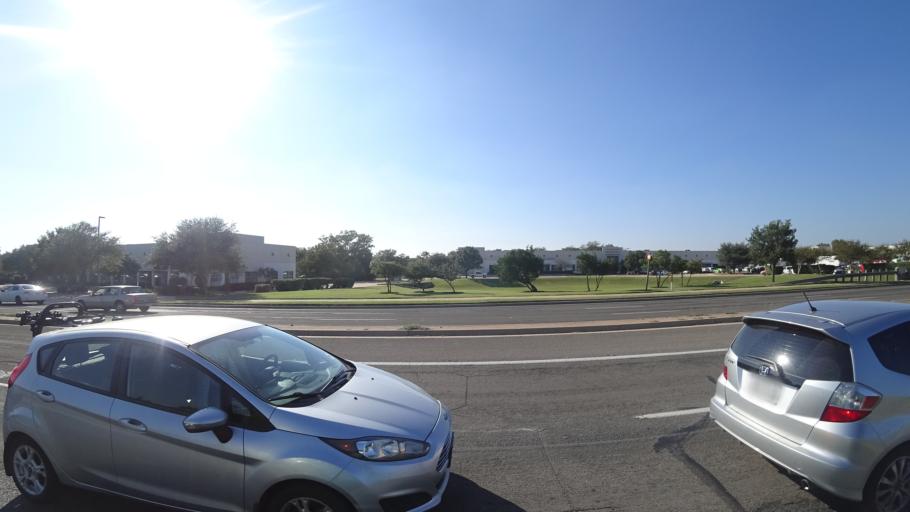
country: US
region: Texas
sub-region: Travis County
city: Wells Branch
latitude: 30.3452
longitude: -97.6775
